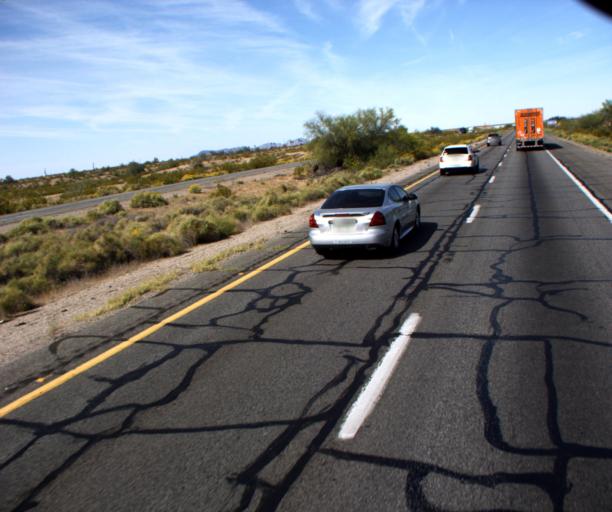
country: US
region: Arizona
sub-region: Maricopa County
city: Buckeye
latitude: 33.4599
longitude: -112.7688
